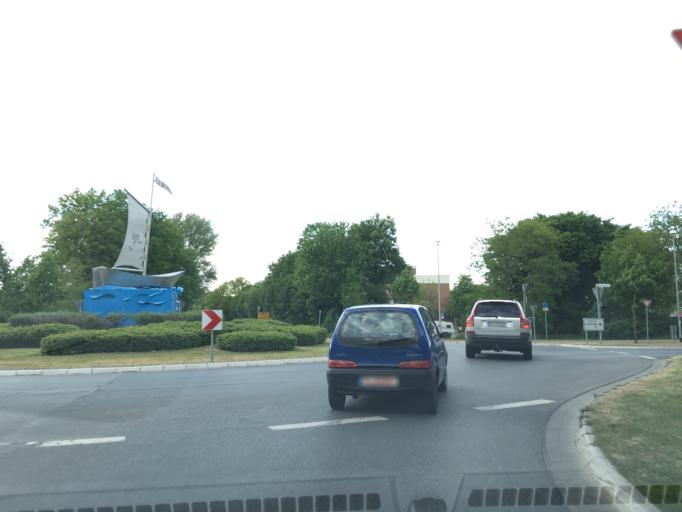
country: DE
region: North Rhine-Westphalia
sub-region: Regierungsbezirk Munster
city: Greven
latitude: 52.0913
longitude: 7.6068
